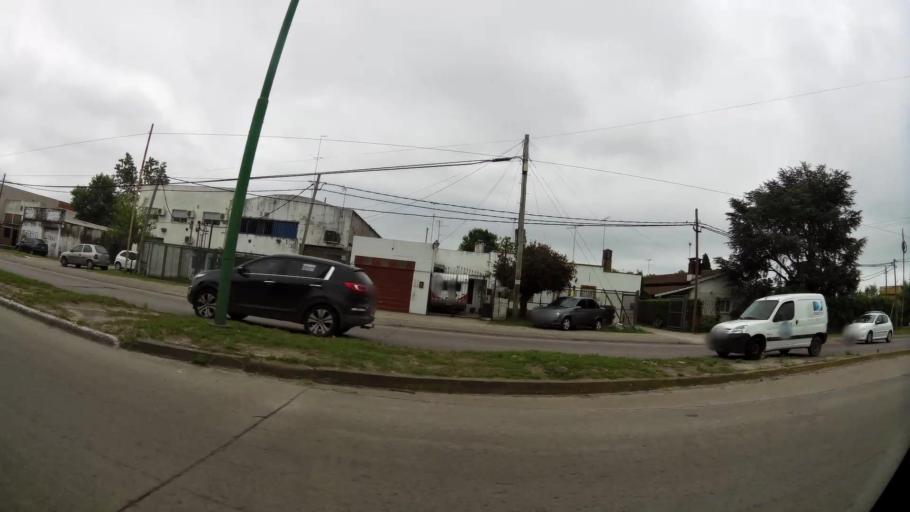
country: AR
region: Buenos Aires
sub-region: Partido de La Plata
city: La Plata
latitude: -34.9732
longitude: -58.0239
